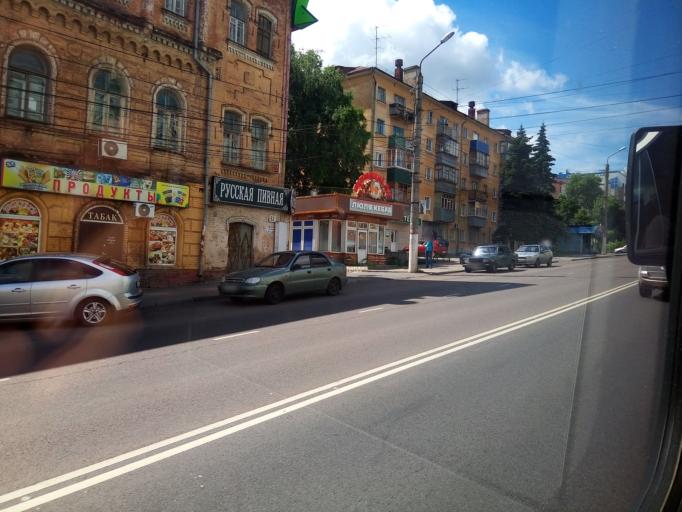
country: RU
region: Kursk
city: Kursk
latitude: 51.7256
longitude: 36.1808
